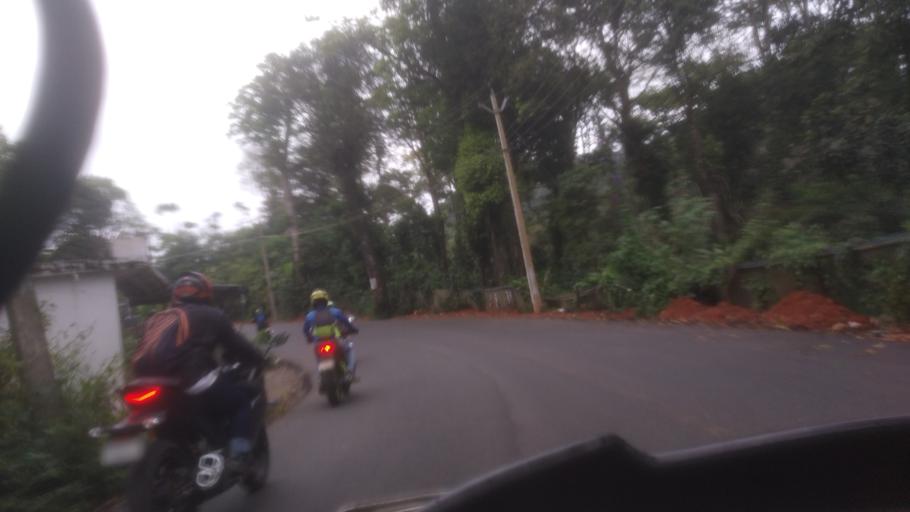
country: IN
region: Tamil Nadu
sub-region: Theni
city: Kombai
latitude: 9.8913
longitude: 77.1551
